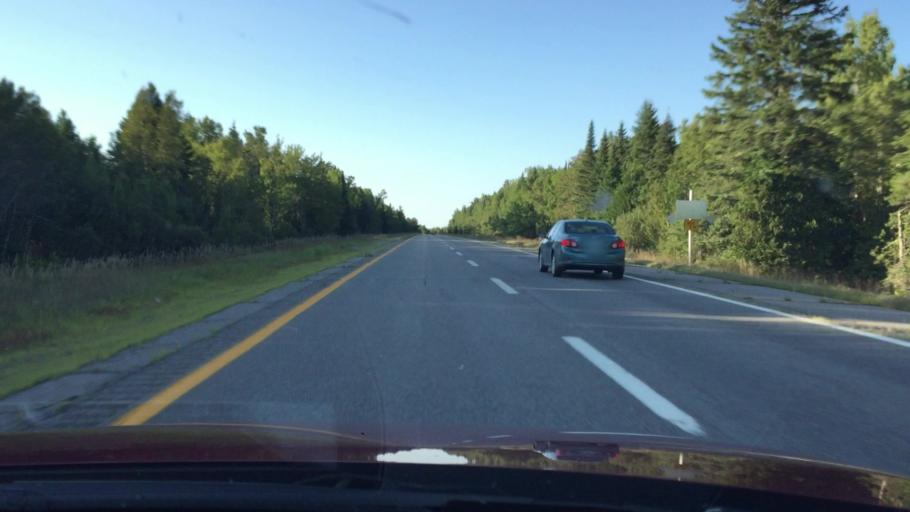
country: US
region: Maine
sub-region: Penobscot County
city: Patten
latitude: 45.8299
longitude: -68.4319
